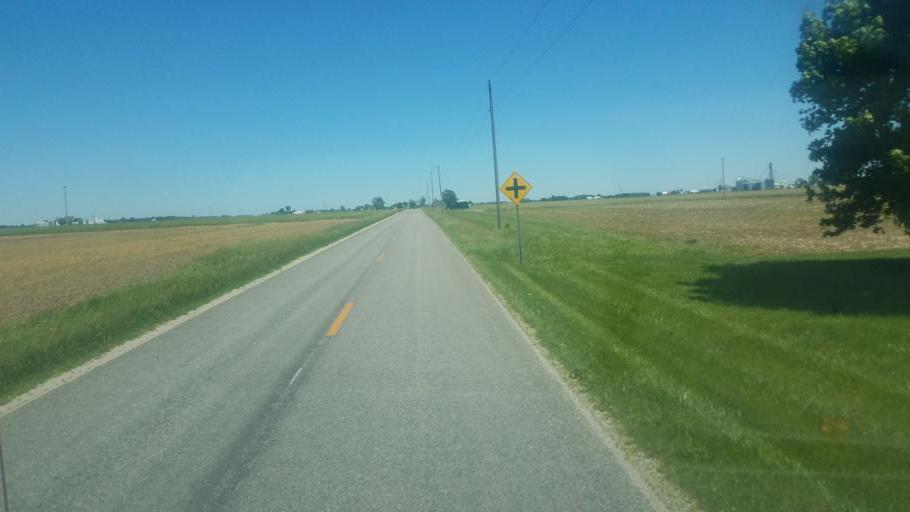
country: US
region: Ohio
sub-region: Shelby County
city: Sidney
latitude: 40.2111
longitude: -84.1169
